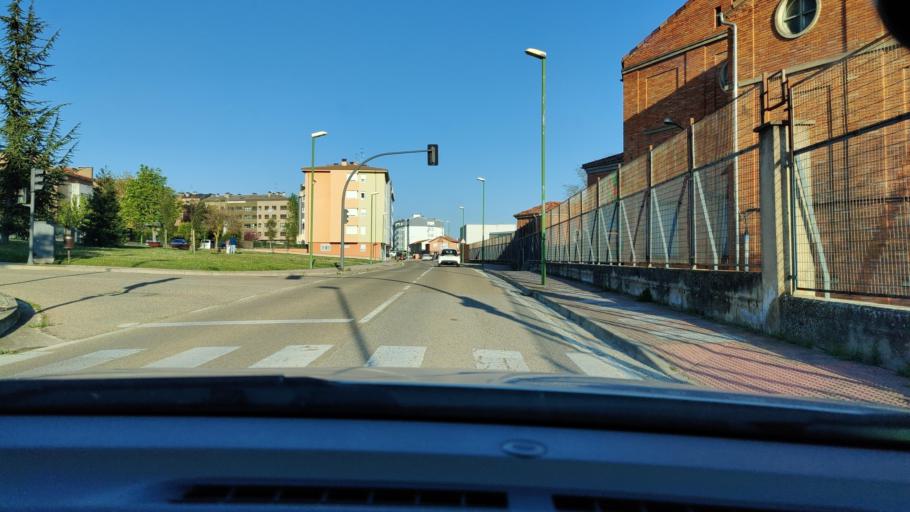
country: ES
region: Castille and Leon
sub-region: Provincia de Burgos
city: Villalbilla de Burgos
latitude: 42.3499
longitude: -3.7363
